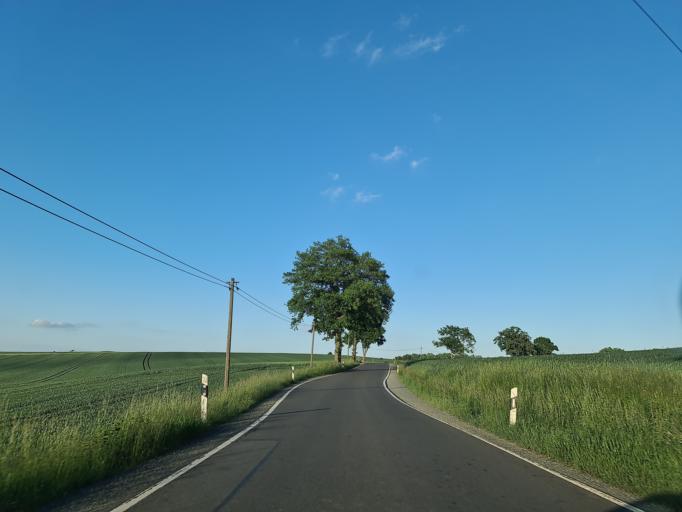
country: DE
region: Saxony
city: Reuth
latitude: 50.4650
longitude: 12.0098
